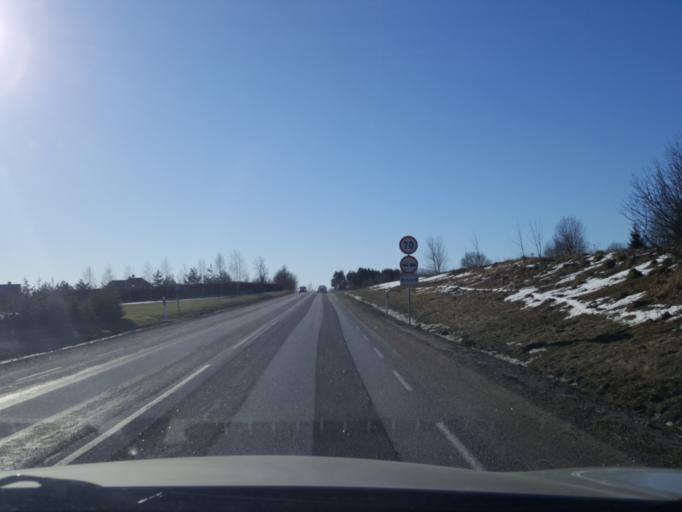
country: EE
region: Viljandimaa
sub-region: Viljandi linn
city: Viljandi
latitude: 58.3828
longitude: 25.6052
